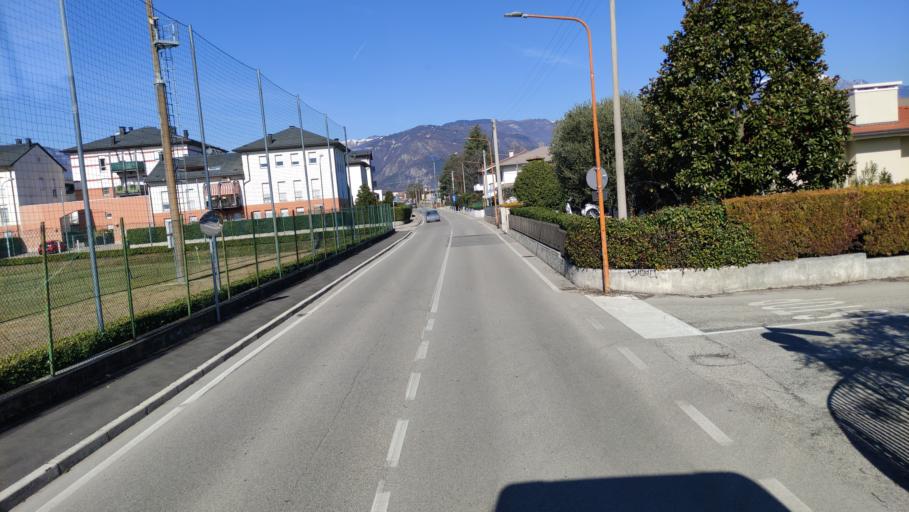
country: IT
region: Veneto
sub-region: Provincia di Vicenza
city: San Zeno-San Giuseppe
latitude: 45.7607
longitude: 11.7532
